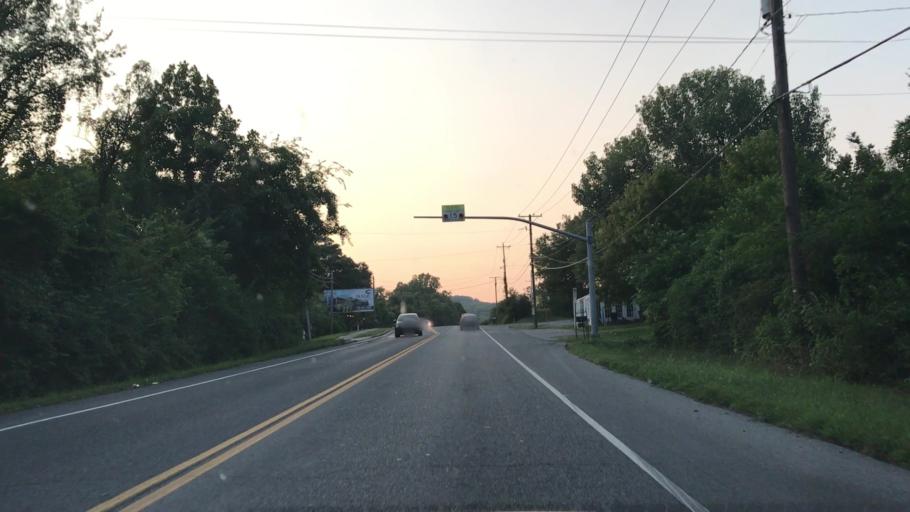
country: US
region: Tennessee
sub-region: Williamson County
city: Brentwood Estates
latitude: 36.0189
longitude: -86.7089
